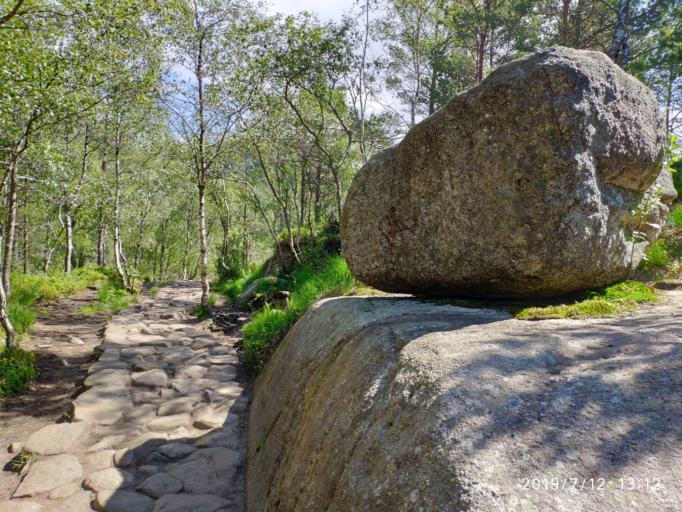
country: NO
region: Rogaland
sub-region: Forsand
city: Forsand
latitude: 58.9893
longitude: 6.1538
